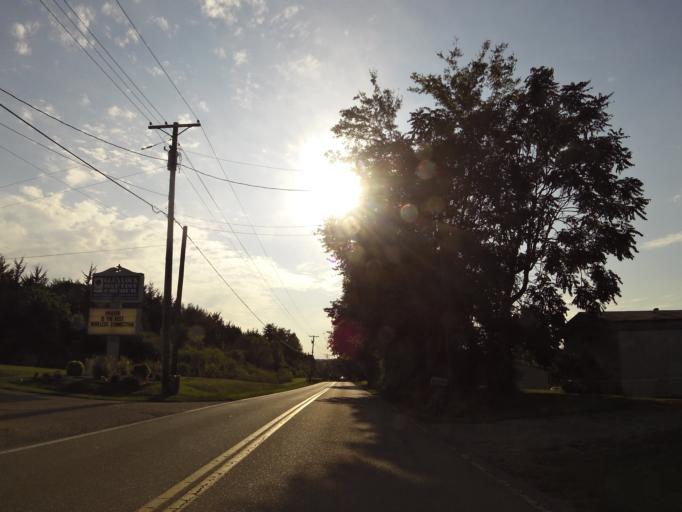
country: US
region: Tennessee
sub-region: Monroe County
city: Madisonville
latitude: 35.6001
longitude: -84.3724
